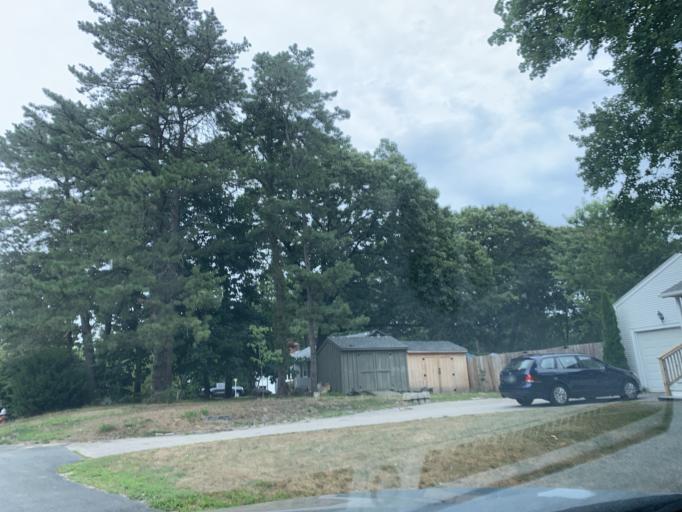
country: US
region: Rhode Island
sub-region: Kent County
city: East Greenwich
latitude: 41.6360
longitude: -71.4614
